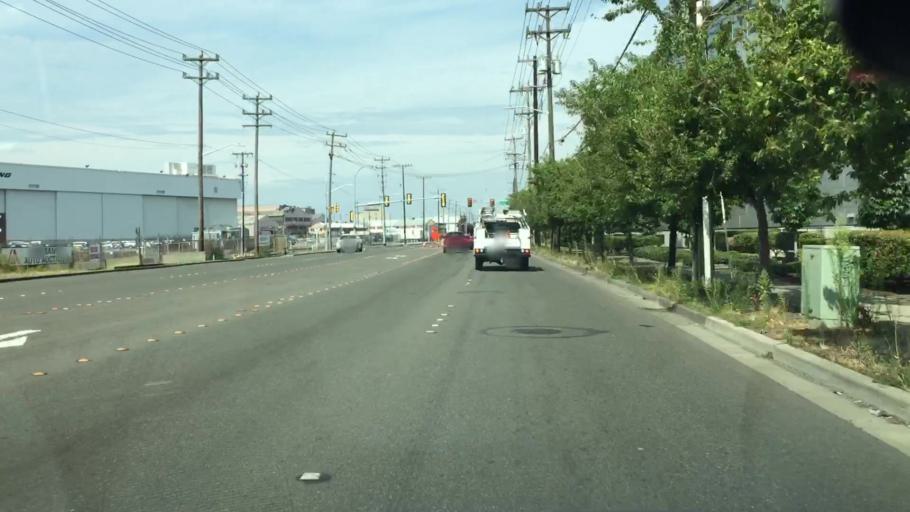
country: US
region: Washington
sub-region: King County
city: Boulevard Park
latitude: 47.5220
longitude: -122.3000
